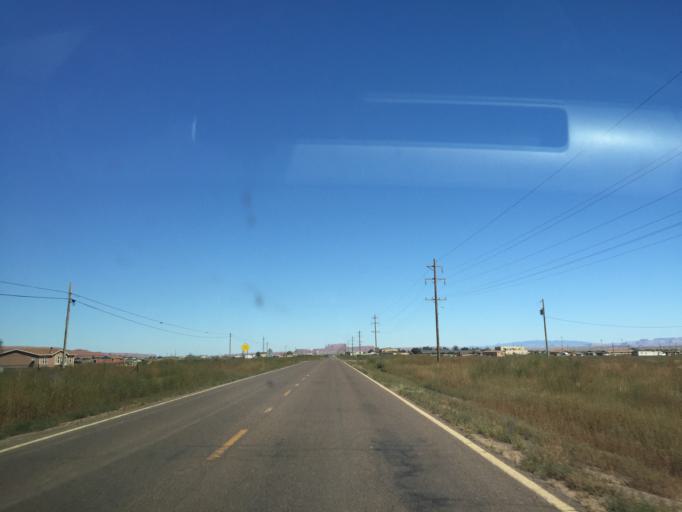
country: US
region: Arizona
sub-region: Apache County
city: Many Farms
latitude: 36.3417
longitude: -109.6227
